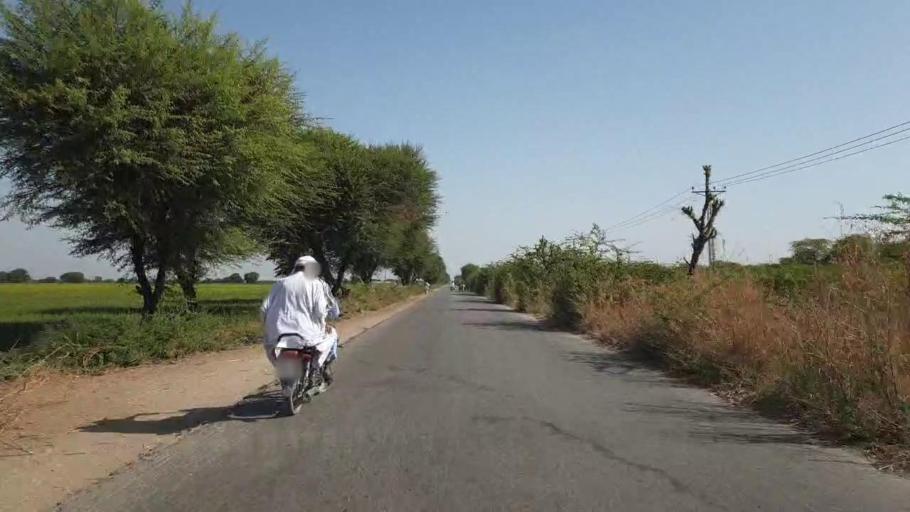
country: PK
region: Sindh
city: Chor
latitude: 25.4412
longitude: 69.7499
